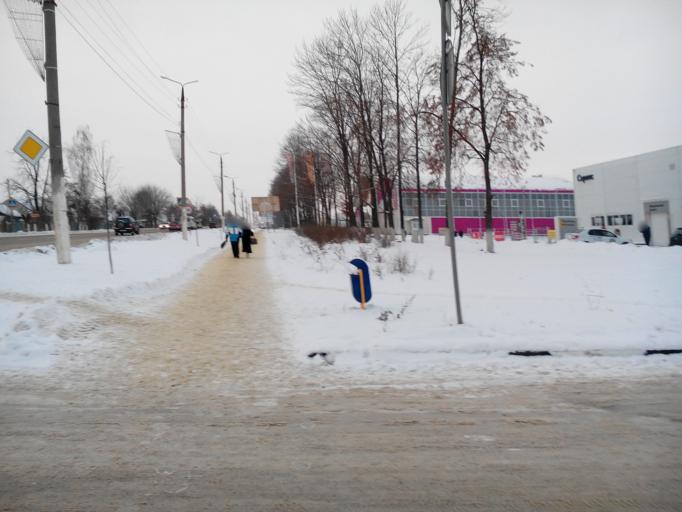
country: RU
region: Tula
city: Yefremov
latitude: 53.1465
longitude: 38.0951
